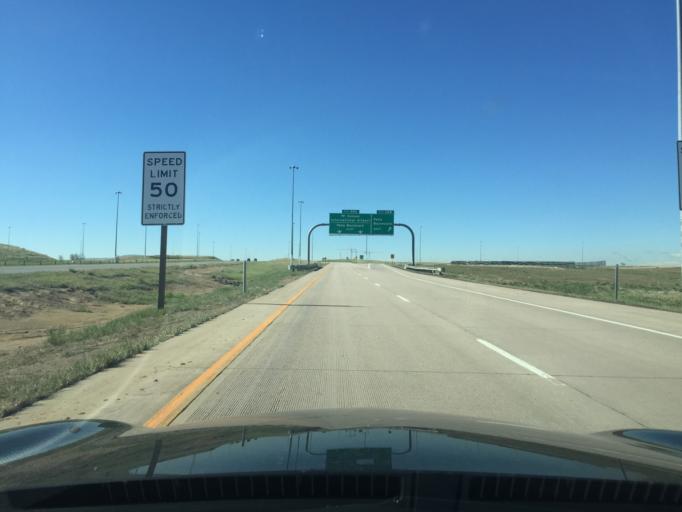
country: US
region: Colorado
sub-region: Adams County
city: Aurora
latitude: 39.8424
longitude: -104.7472
